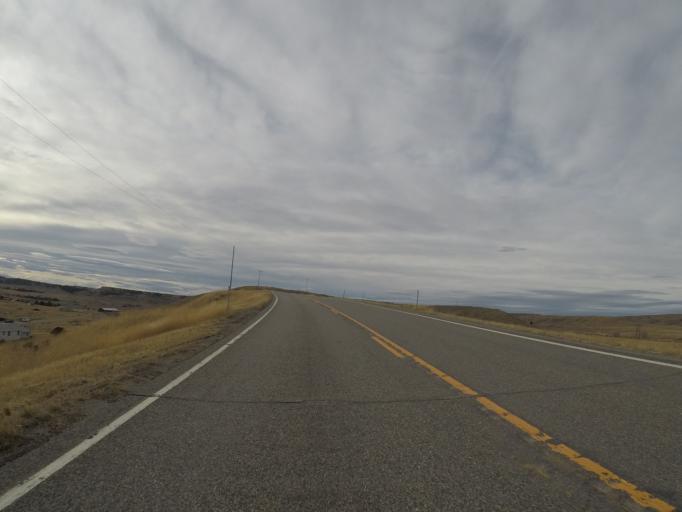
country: US
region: Montana
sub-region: Yellowstone County
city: Laurel
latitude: 45.8453
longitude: -108.7309
